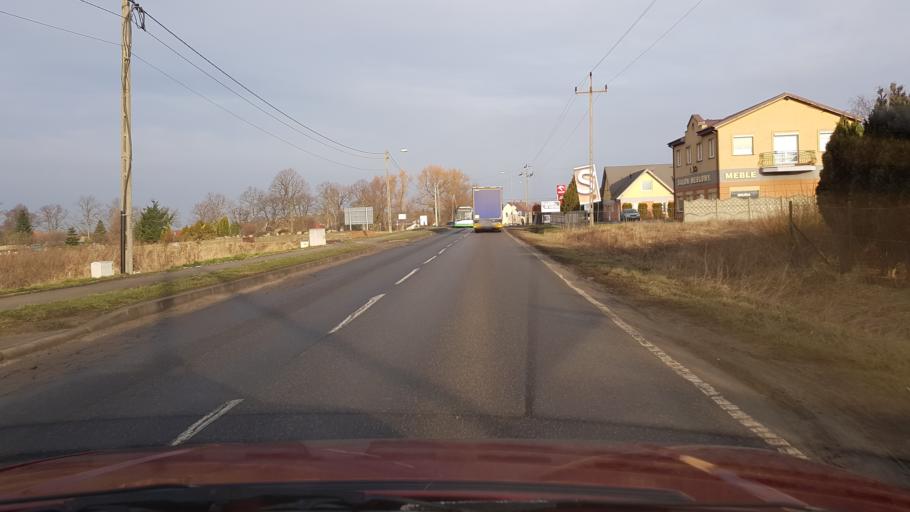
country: PL
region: West Pomeranian Voivodeship
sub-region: Powiat policki
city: Police
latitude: 53.5135
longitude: 14.5679
